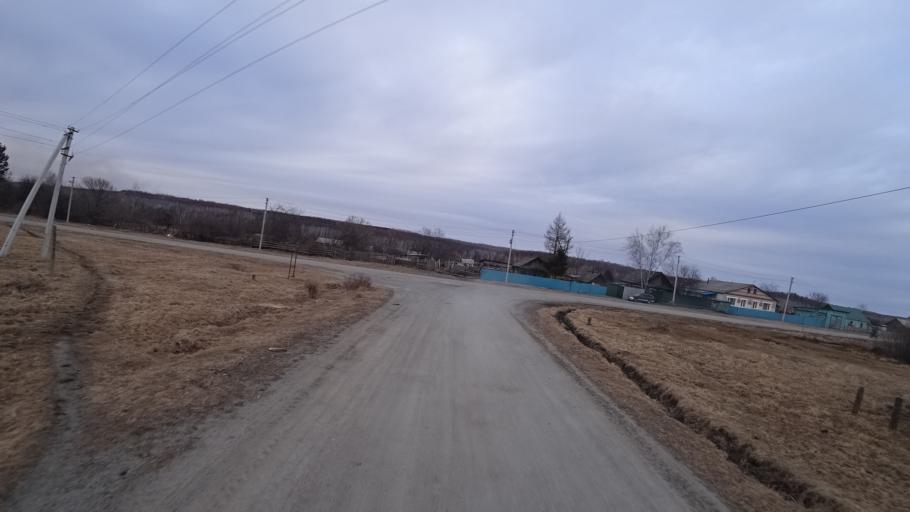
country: RU
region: Amur
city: Bureya
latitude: 50.0197
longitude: 129.7687
